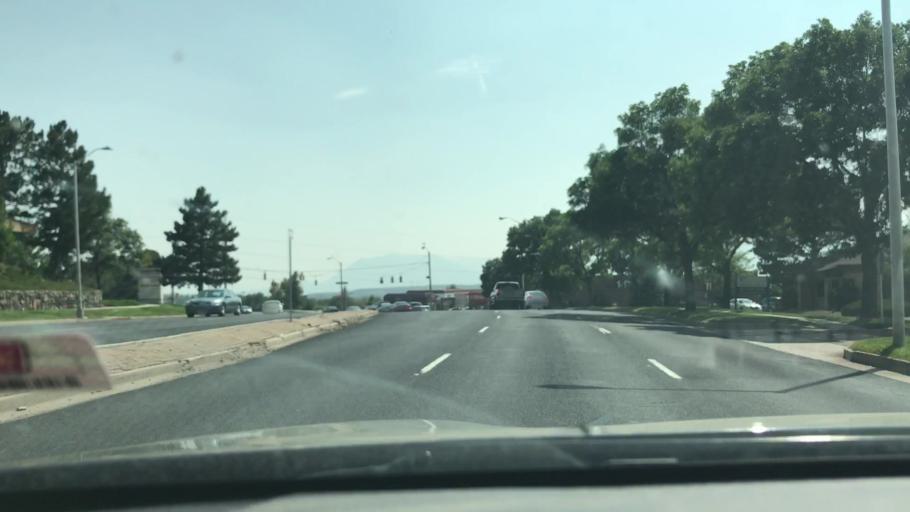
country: US
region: Colorado
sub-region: El Paso County
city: Black Forest
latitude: 38.9429
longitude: -104.7748
